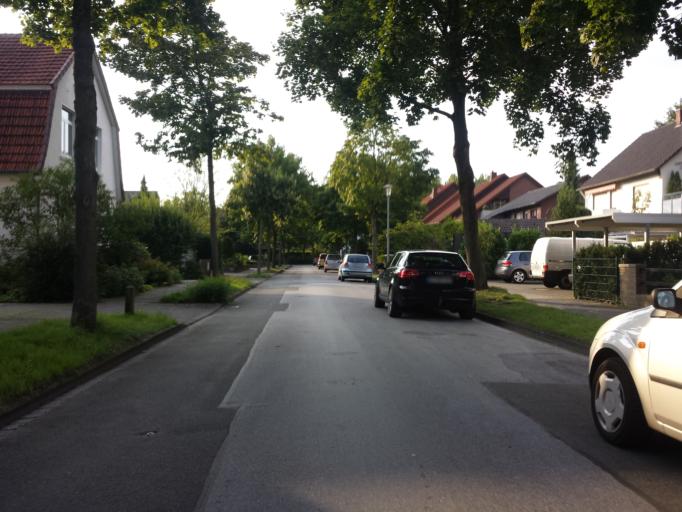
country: DE
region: North Rhine-Westphalia
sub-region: Regierungsbezirk Detmold
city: Guetersloh
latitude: 51.9094
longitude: 8.3642
